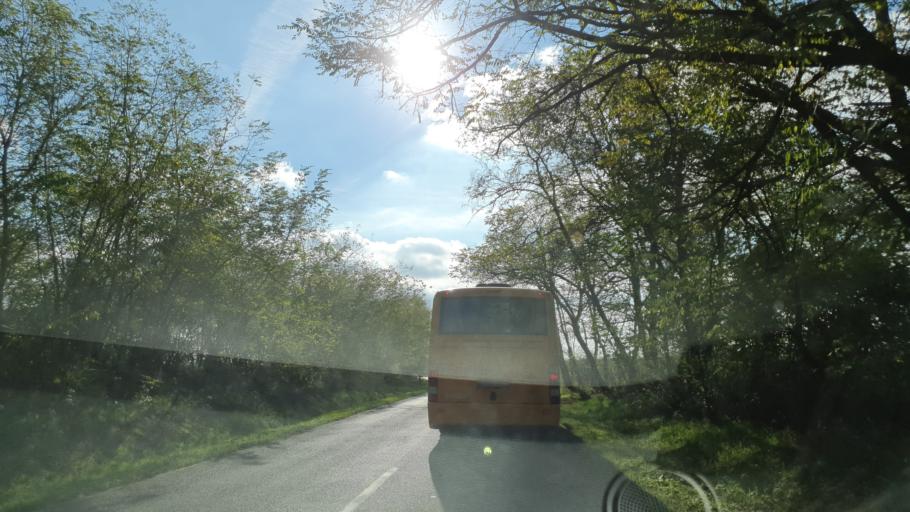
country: HU
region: Szabolcs-Szatmar-Bereg
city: Gyulahaza
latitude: 48.1226
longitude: 22.0886
